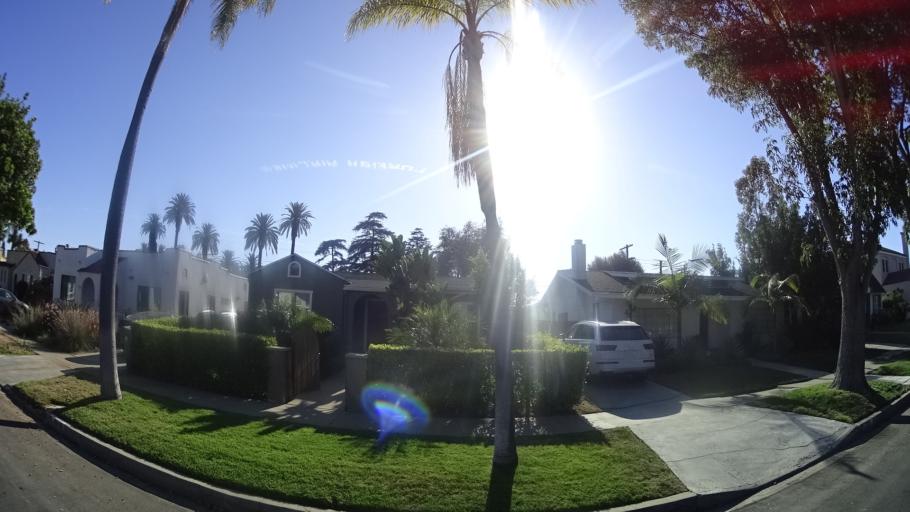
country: US
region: California
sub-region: Los Angeles County
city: Hollywood
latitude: 34.0774
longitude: -118.3187
